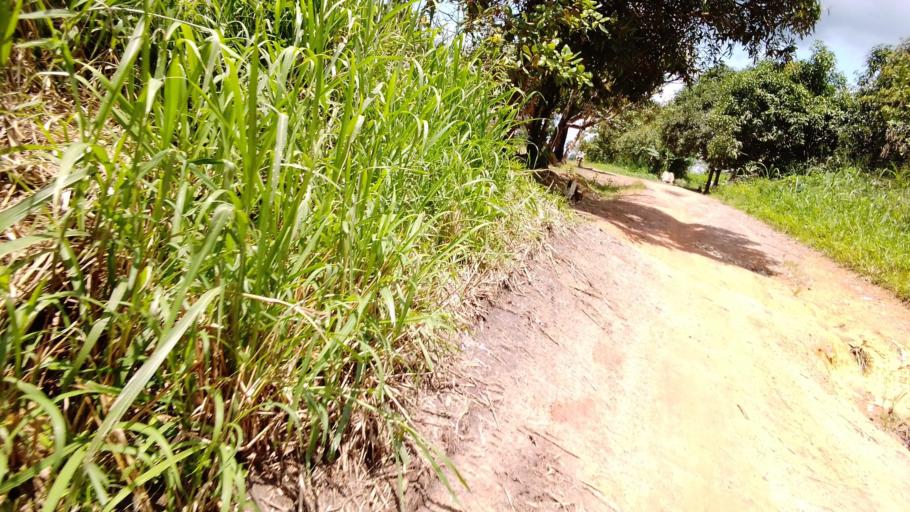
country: SL
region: Eastern Province
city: Koidu
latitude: 8.6893
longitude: -10.9554
